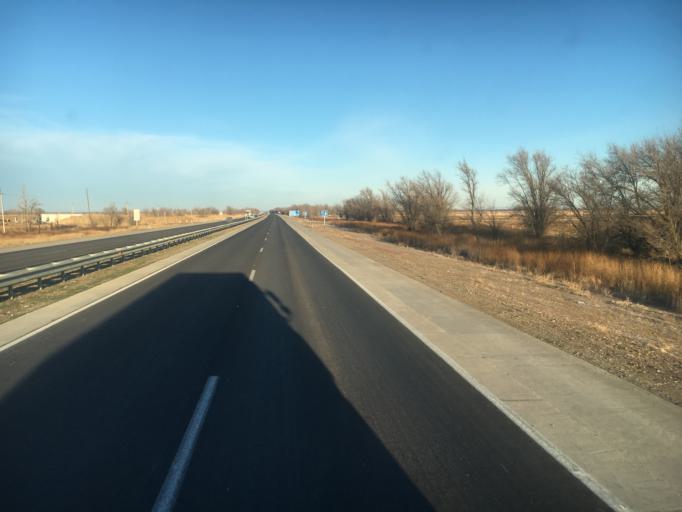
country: KZ
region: Ongtustik Qazaqstan
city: Bayaldyr
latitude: 43.0927
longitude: 68.6378
